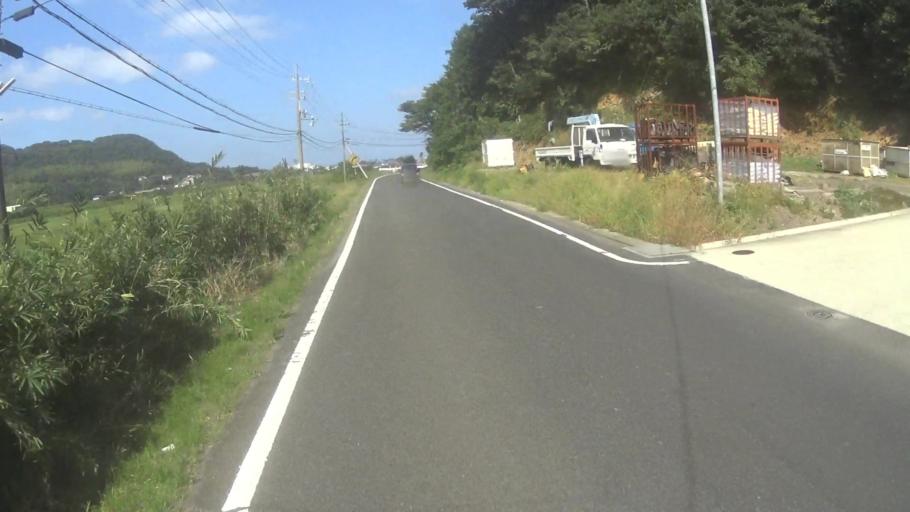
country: JP
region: Kyoto
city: Miyazu
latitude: 35.7305
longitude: 135.1036
